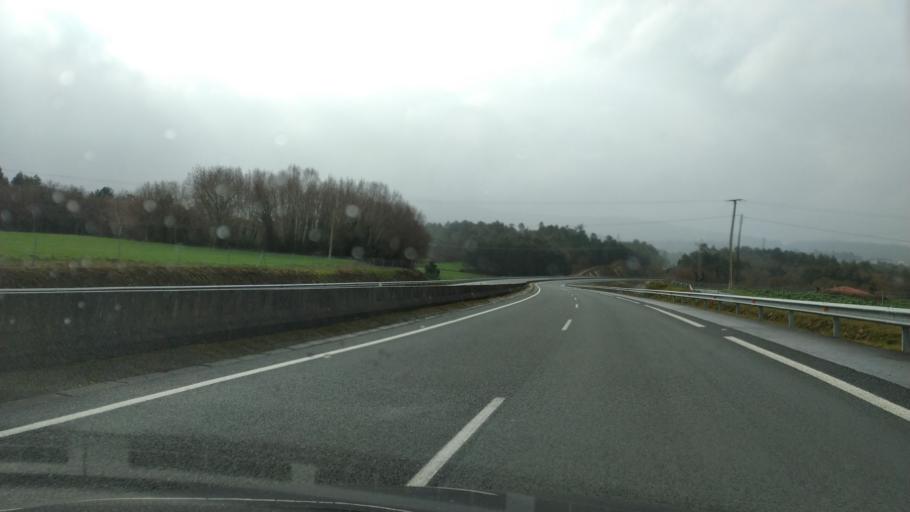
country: ES
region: Galicia
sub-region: Provincia de Pontevedra
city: Silleda
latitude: 42.7188
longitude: -8.2648
